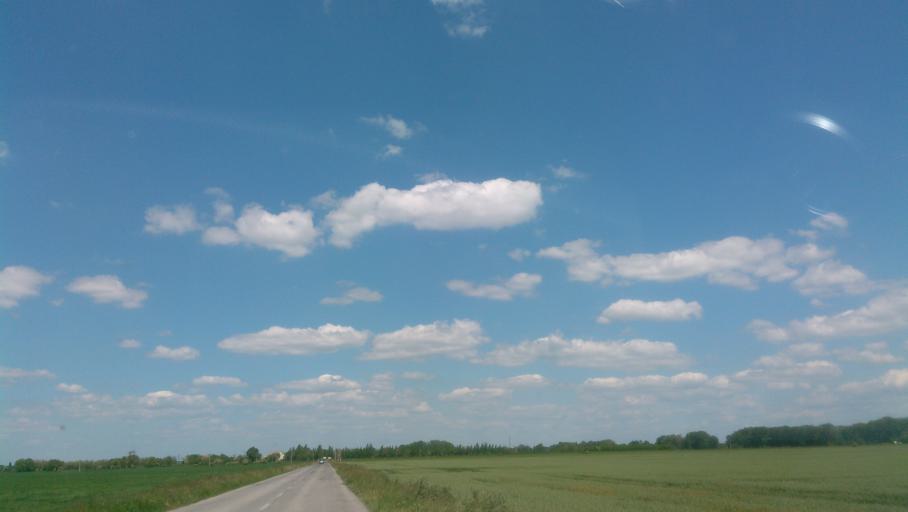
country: SK
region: Trnavsky
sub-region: Okres Dunajska Streda
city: Velky Meder
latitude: 47.9035
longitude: 17.8551
